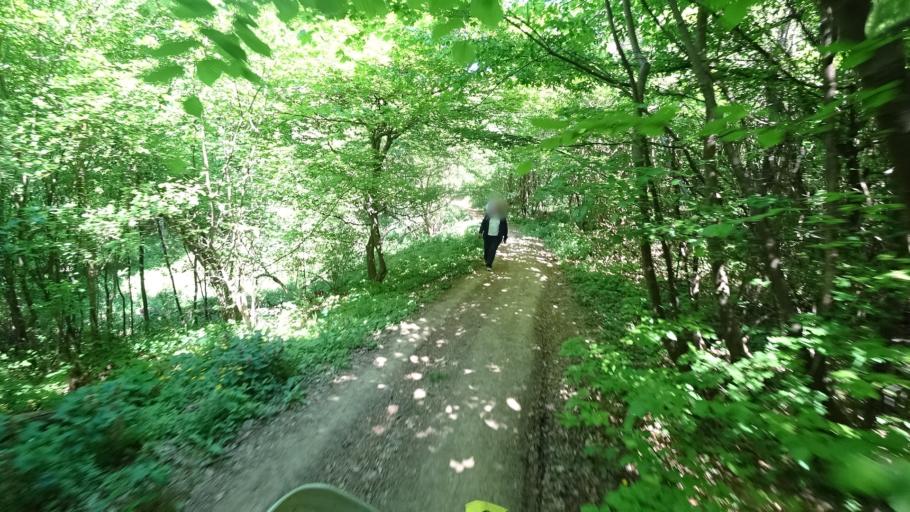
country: HR
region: Zagrebacka
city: Jablanovec
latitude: 45.8519
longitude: 15.8578
